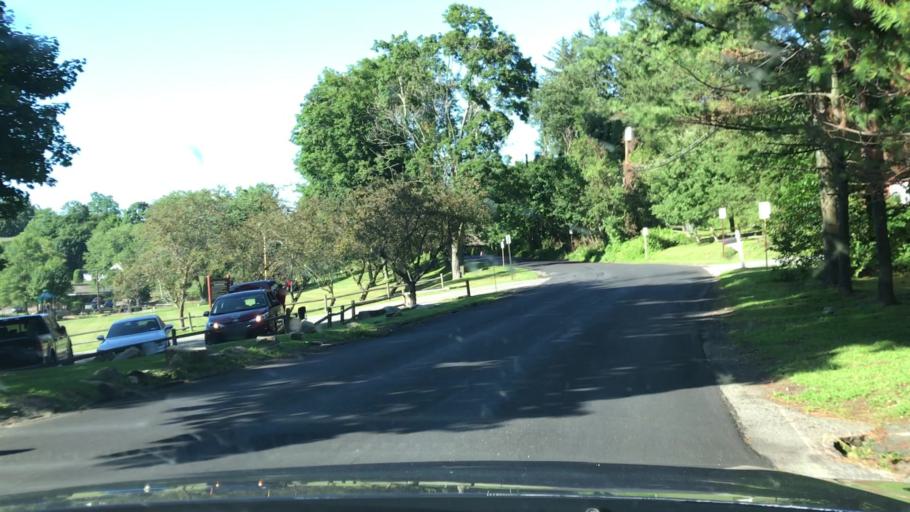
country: US
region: New York
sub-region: Westchester County
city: Thornwood
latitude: 41.1165
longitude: -73.7744
